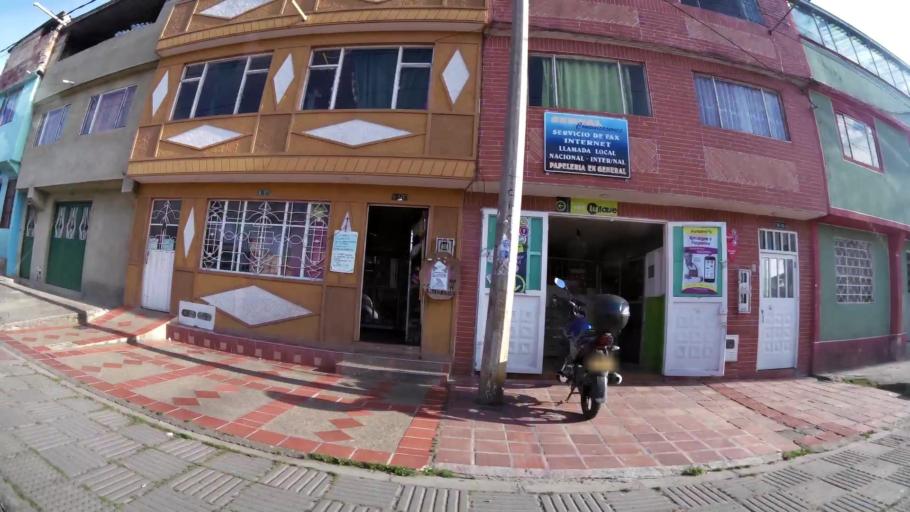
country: CO
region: Bogota D.C.
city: Bogota
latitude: 4.5423
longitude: -74.0932
